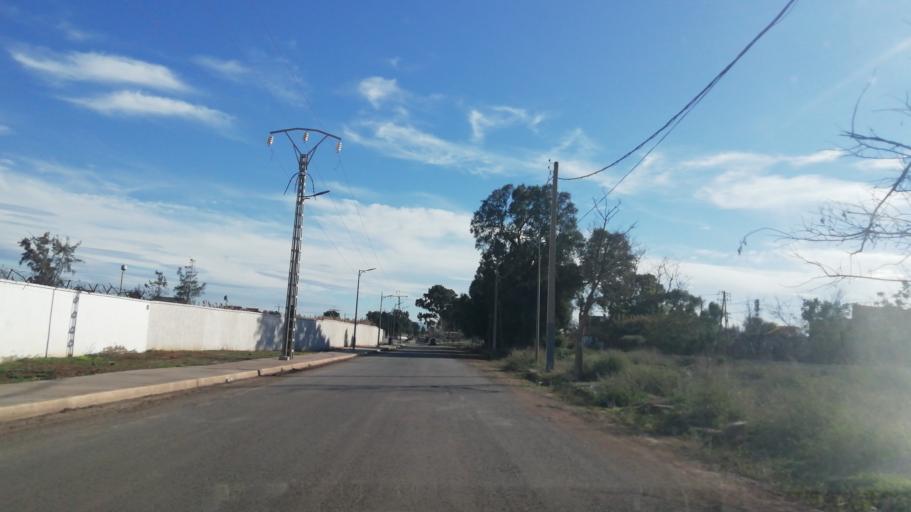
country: DZ
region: Oran
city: Es Senia
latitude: 35.6187
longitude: -0.5861
